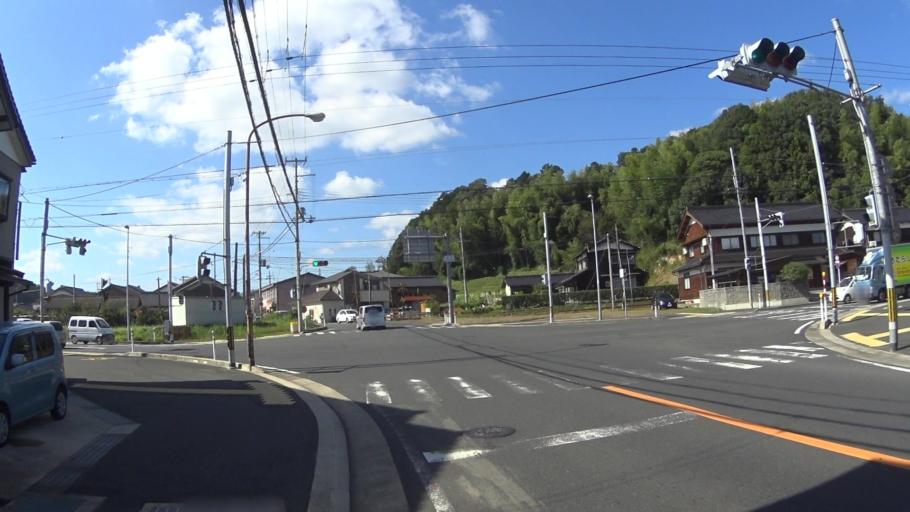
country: JP
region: Kyoto
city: Miyazu
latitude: 35.6290
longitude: 135.0720
